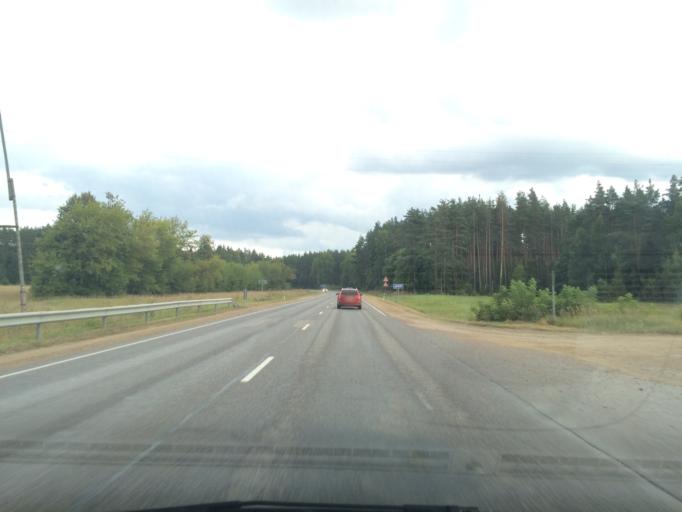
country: LV
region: Koknese
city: Koknese
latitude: 56.6011
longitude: 25.5183
